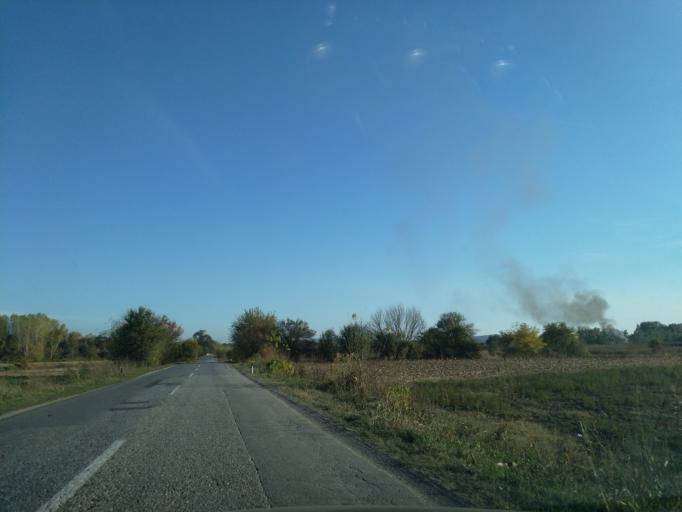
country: RS
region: Central Serbia
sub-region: Pomoravski Okrug
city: Svilajnac
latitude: 44.2320
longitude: 21.1415
